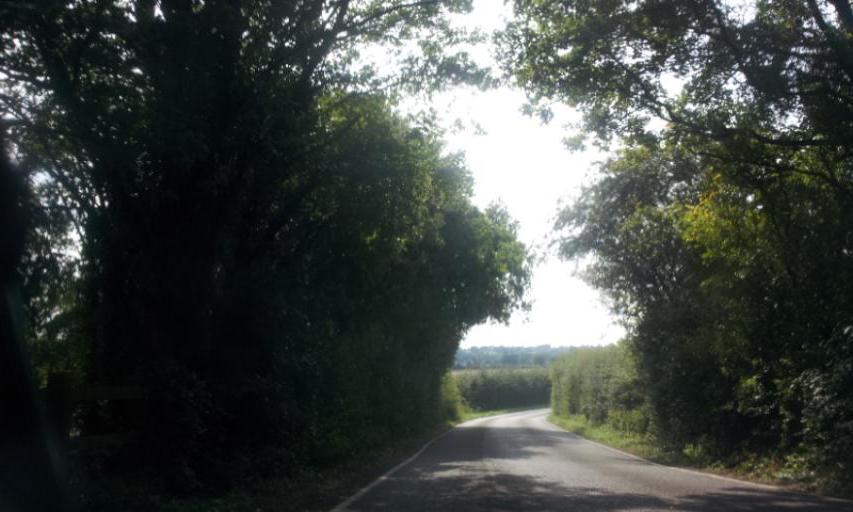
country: GB
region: England
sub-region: Kent
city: Paddock Wood
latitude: 51.1765
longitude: 0.4112
